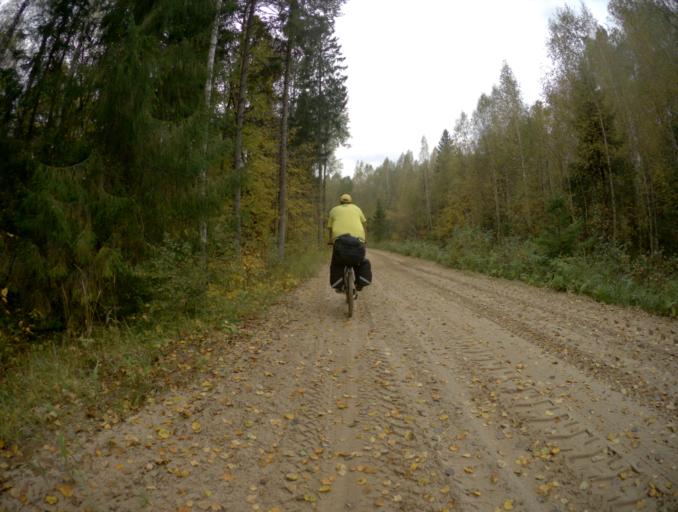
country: RU
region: Vladimir
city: Kideksha
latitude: 56.5002
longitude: 40.7573
